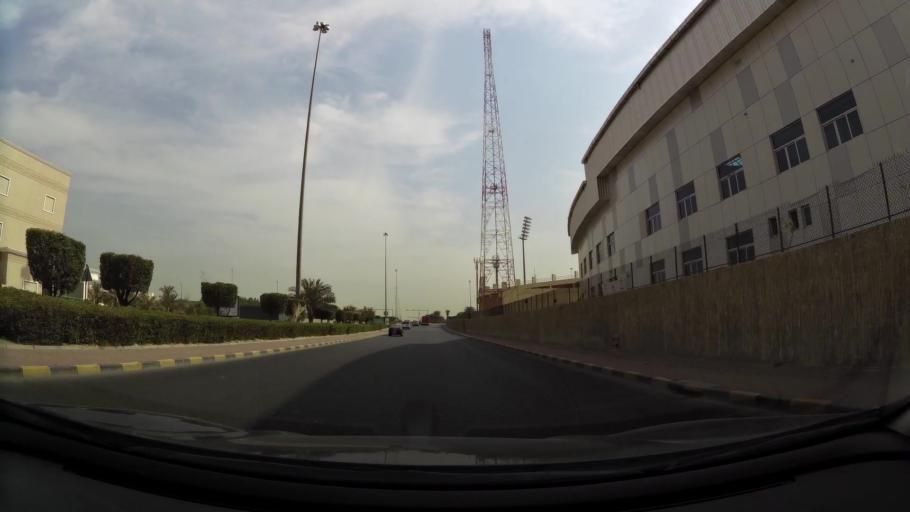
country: KW
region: Al Farwaniyah
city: Janub as Surrah
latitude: 29.2833
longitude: 47.9822
